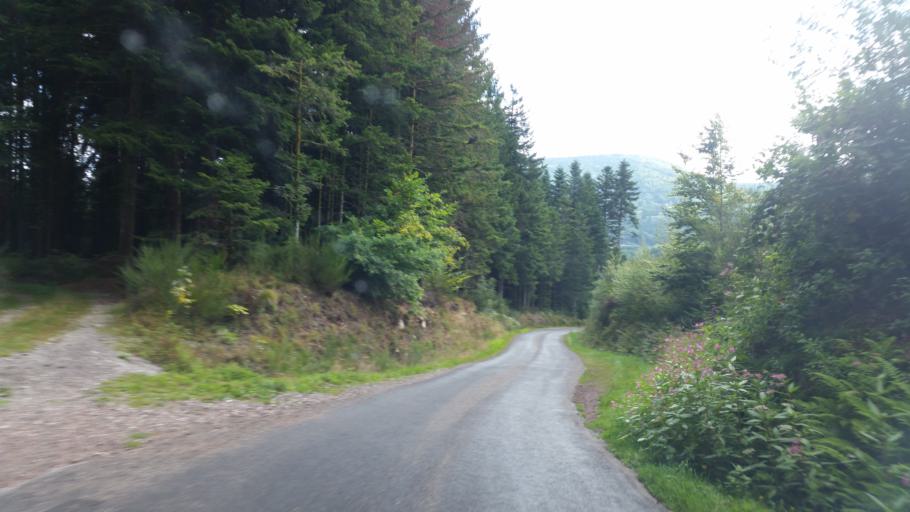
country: FR
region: Lorraine
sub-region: Departement des Vosges
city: Vecoux
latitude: 47.9863
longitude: 6.6151
